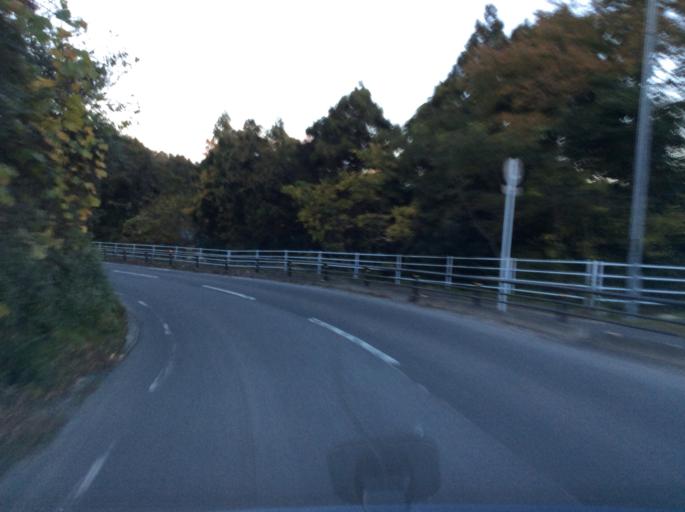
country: JP
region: Fukushima
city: Iwaki
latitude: 37.1275
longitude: 140.8536
